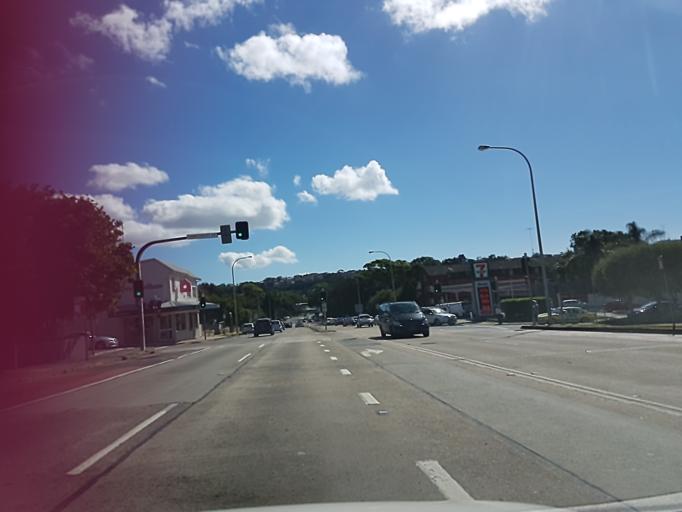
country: AU
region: New South Wales
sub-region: Warringah
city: Dee Why
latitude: -33.7497
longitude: 151.2895
